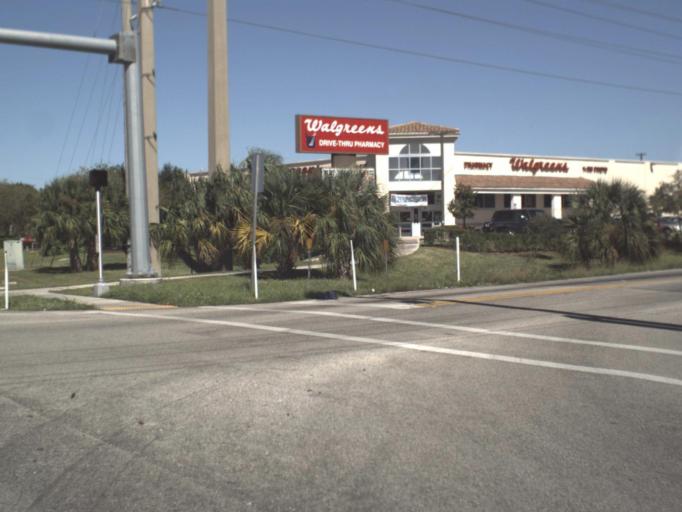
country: US
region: Florida
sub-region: Lee County
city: Palmona Park
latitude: 26.6967
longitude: -81.9006
